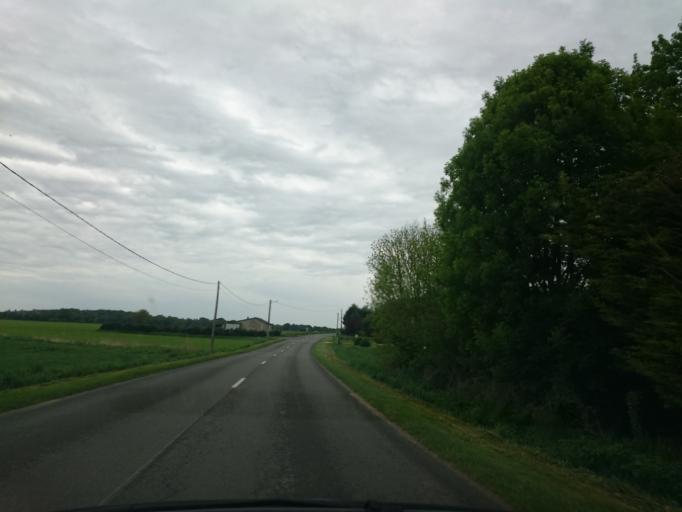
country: FR
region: Centre
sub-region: Departement du Loir-et-Cher
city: Muides-sur-Loire
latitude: 47.6673
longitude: 1.5329
